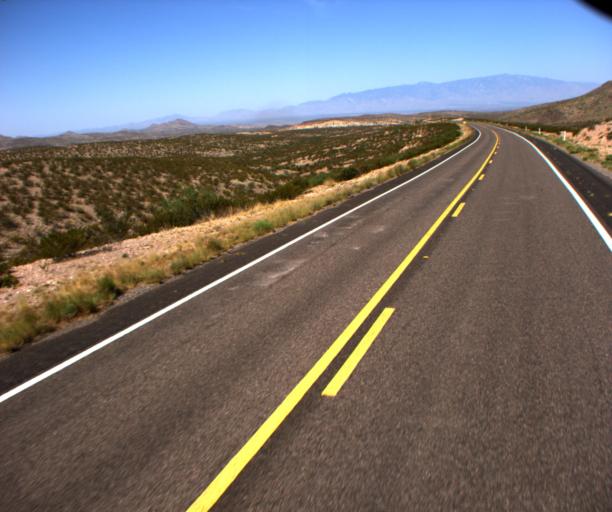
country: US
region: Arizona
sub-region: Greenlee County
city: Clifton
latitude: 32.7541
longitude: -109.3683
